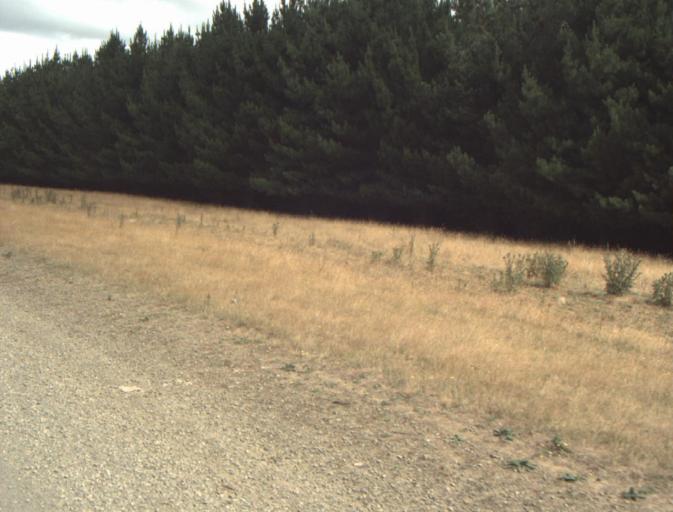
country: AU
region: Tasmania
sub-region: Dorset
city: Scottsdale
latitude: -41.4687
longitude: 147.5990
